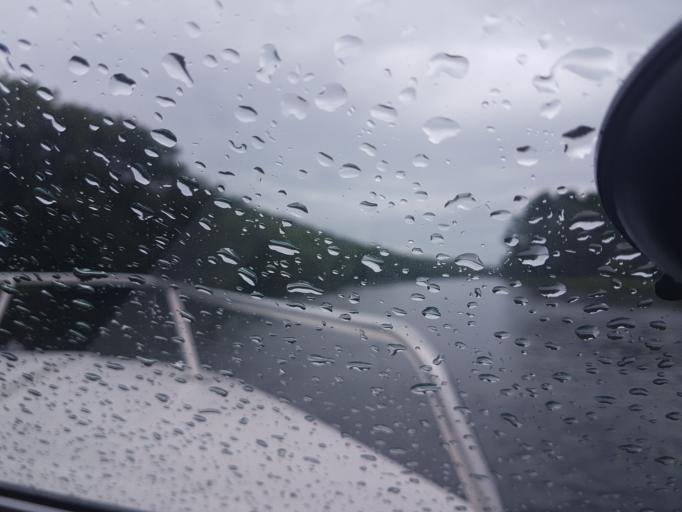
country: FR
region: Bourgogne
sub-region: Departement de l'Yonne
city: Saint-Bris-le-Vineux
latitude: 47.7205
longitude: 3.6299
